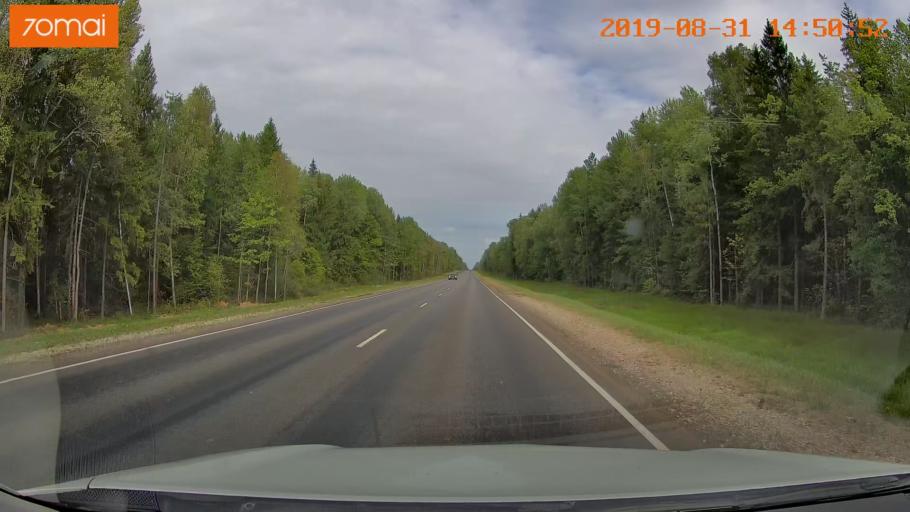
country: RU
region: Kaluga
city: Spas-Demensk
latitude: 54.2646
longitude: 33.8006
